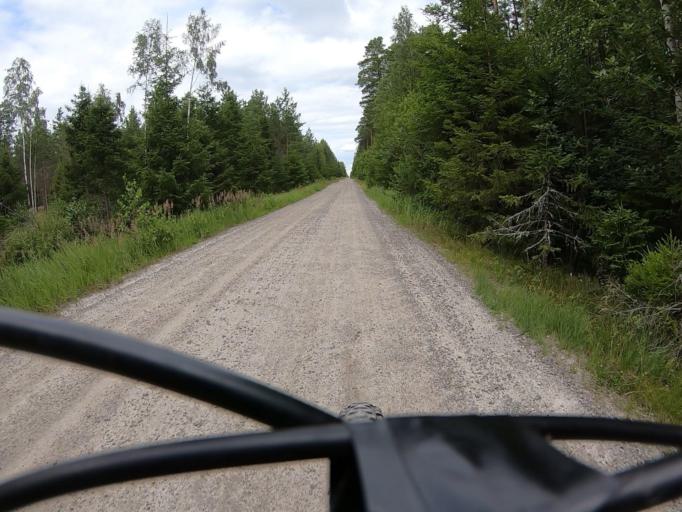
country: FI
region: Varsinais-Suomi
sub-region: Vakka-Suomi
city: Uusikaupunki
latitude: 60.8515
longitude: 21.3791
